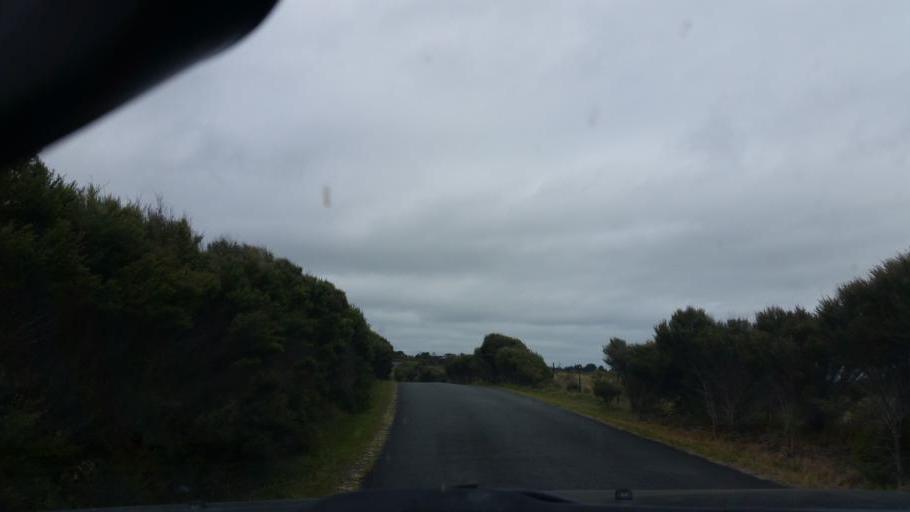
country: NZ
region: Northland
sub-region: Kaipara District
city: Dargaville
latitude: -35.8129
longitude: 173.6478
